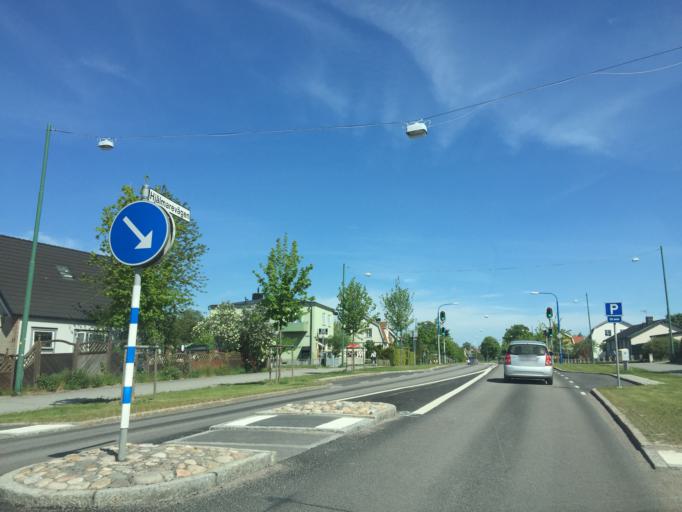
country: SE
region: OErebro
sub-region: Orebro Kommun
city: Orebro
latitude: 59.2613
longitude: 15.2444
